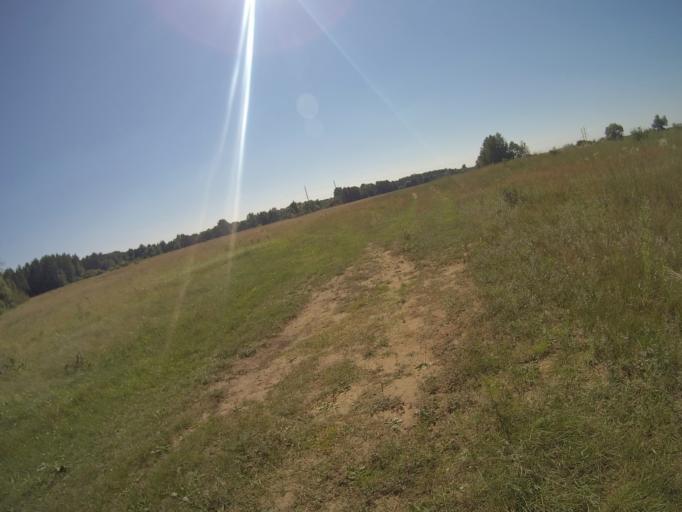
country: RU
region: Vladimir
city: Raduzhnyy
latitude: 56.0315
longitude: 40.2475
